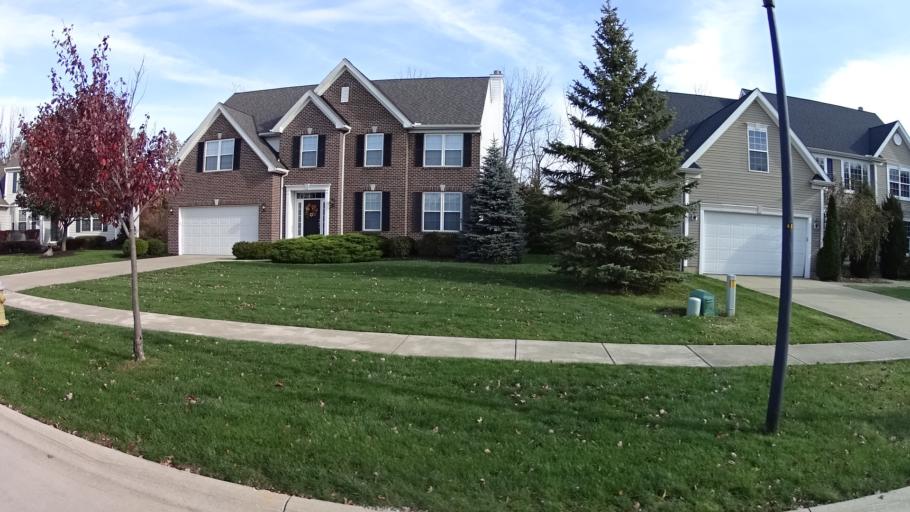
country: US
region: Ohio
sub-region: Lorain County
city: Avon Lake
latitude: 41.4966
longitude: -82.0368
